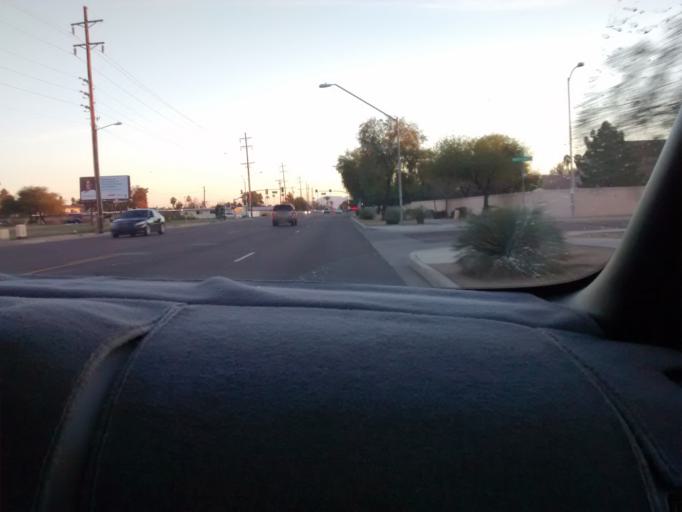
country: US
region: Arizona
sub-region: Maricopa County
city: Glendale
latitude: 33.5434
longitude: -112.2032
